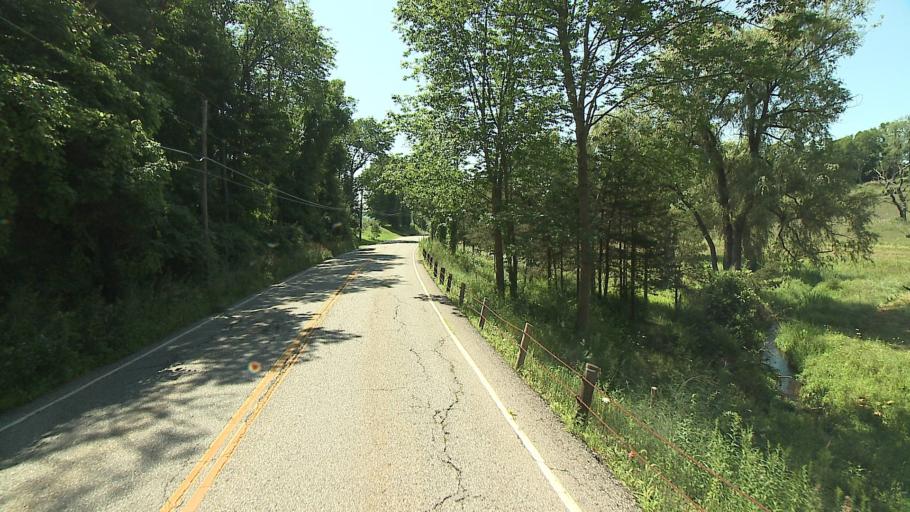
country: US
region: Connecticut
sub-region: Litchfield County
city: Kent
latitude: 41.9003
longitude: -73.4886
